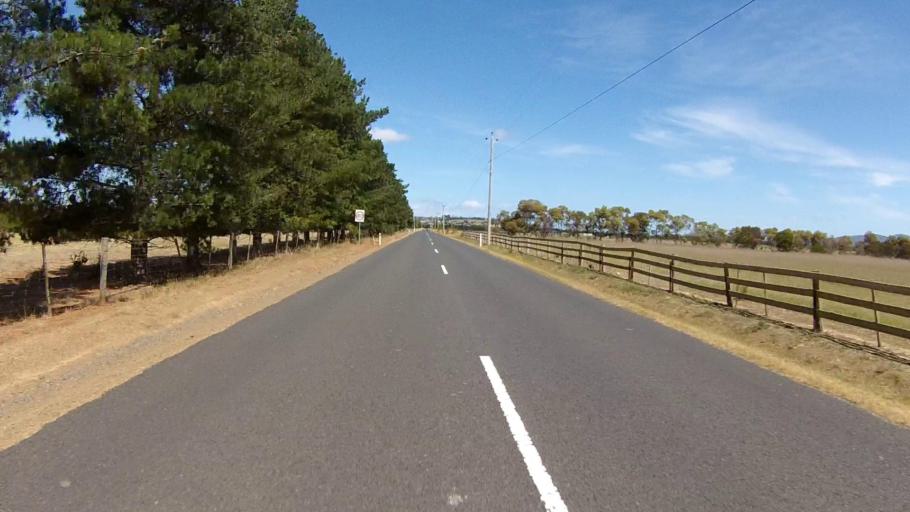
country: AU
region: Tasmania
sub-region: Sorell
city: Sorell
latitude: -42.7711
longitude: 147.5175
